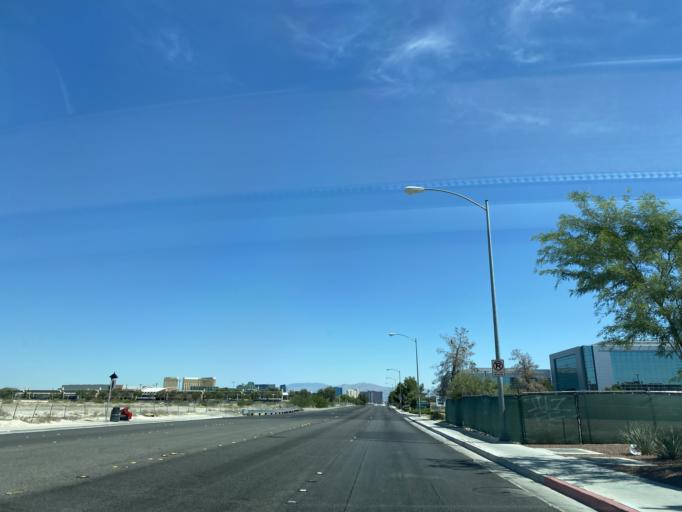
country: US
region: Nevada
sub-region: Clark County
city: Paradise
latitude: 36.0650
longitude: -115.1633
